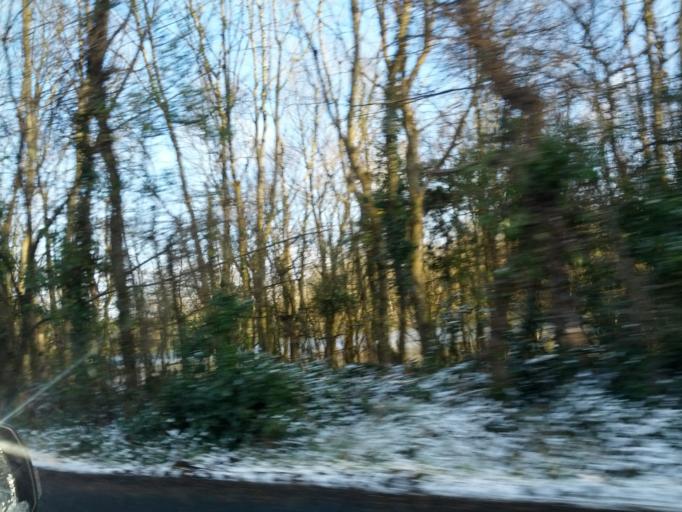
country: IE
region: Connaught
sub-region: County Galway
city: Gort
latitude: 53.1547
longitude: -8.7870
